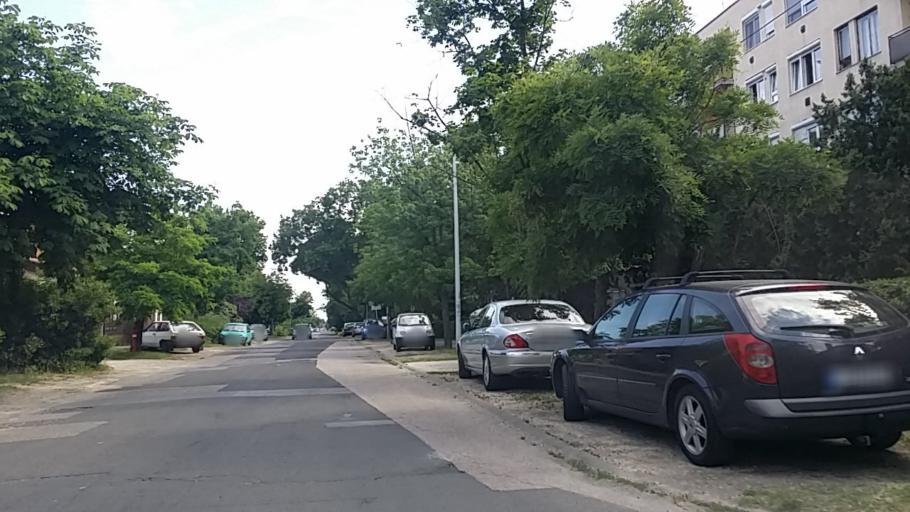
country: HU
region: Budapest
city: Budapest XXI. keruelet
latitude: 47.4259
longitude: 19.0782
